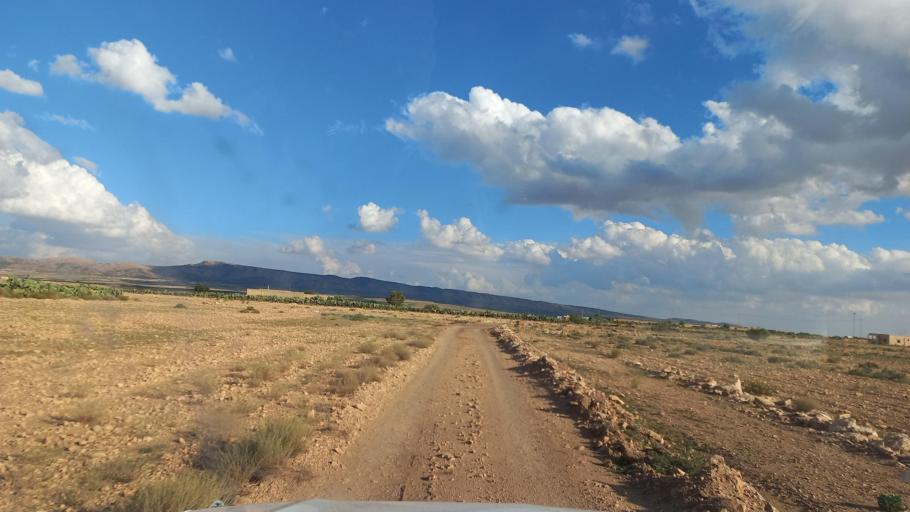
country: TN
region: Al Qasrayn
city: Sbiba
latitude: 35.3849
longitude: 9.0691
